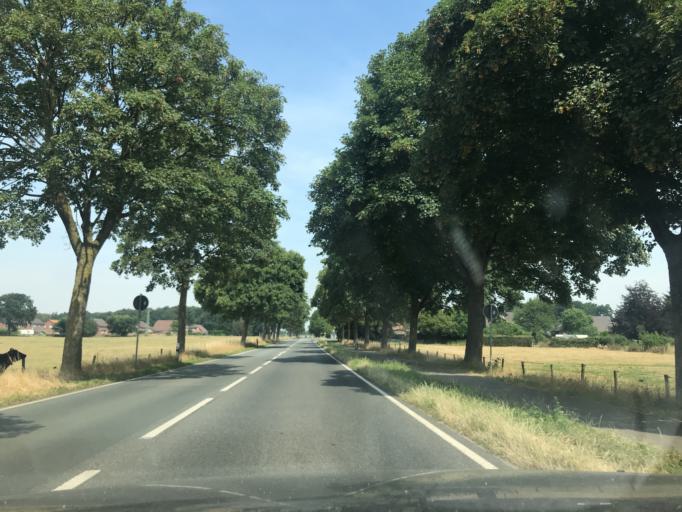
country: DE
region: North Rhine-Westphalia
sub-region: Regierungsbezirk Dusseldorf
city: Issum
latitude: 51.4959
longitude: 6.4179
